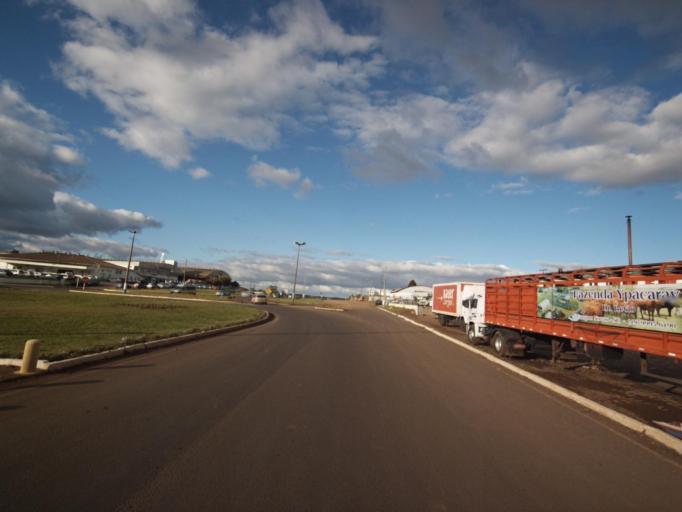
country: BR
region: Santa Catarina
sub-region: Campos Novos
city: Campos Novos
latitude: -27.3908
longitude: -51.2156
